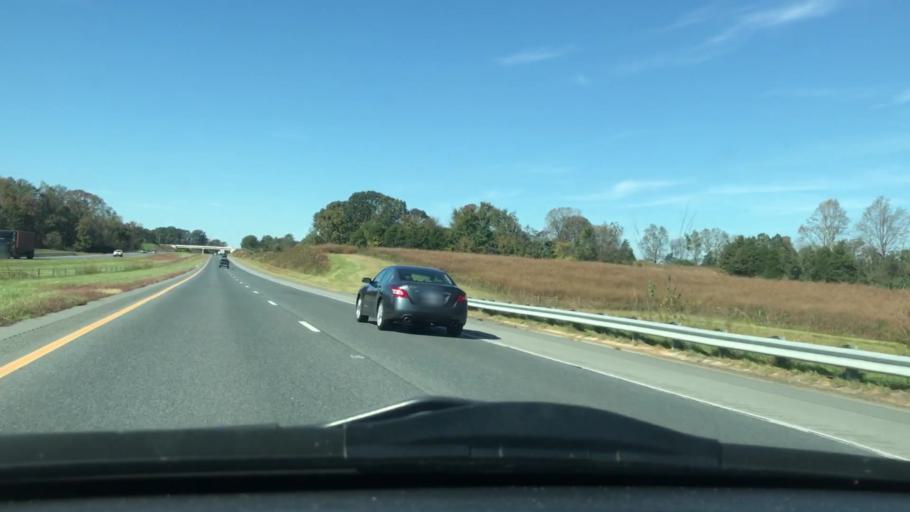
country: US
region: North Carolina
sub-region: Randolph County
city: Randleman
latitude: 35.8500
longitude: -79.8742
